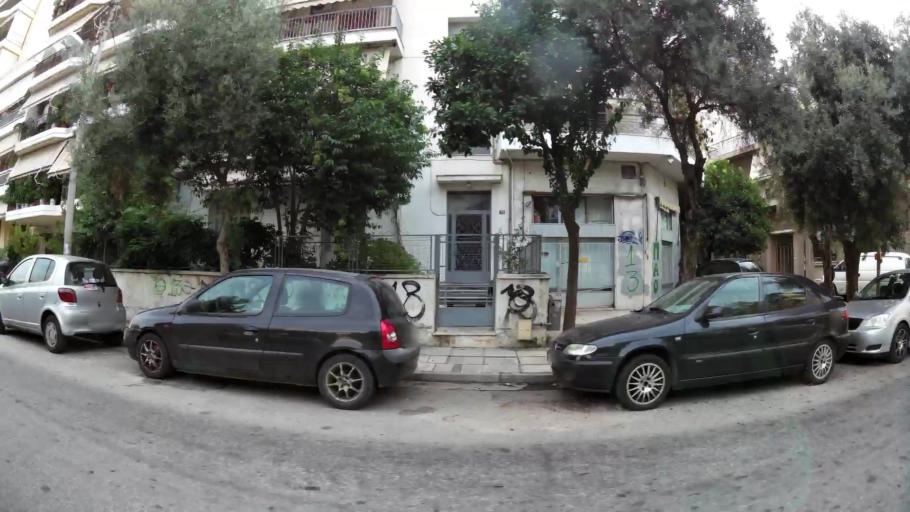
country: GR
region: Attica
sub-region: Nomarchia Athinas
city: Nea Chalkidona
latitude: 38.0160
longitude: 23.7230
